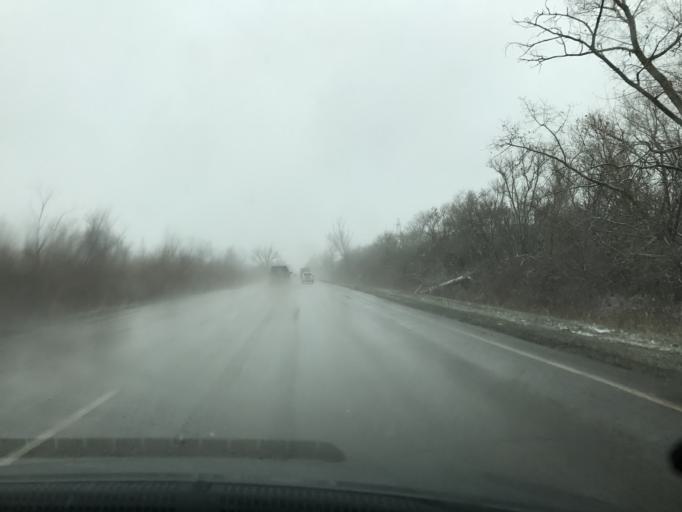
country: RU
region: Rostov
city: Bataysk
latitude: 47.0520
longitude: 39.8345
